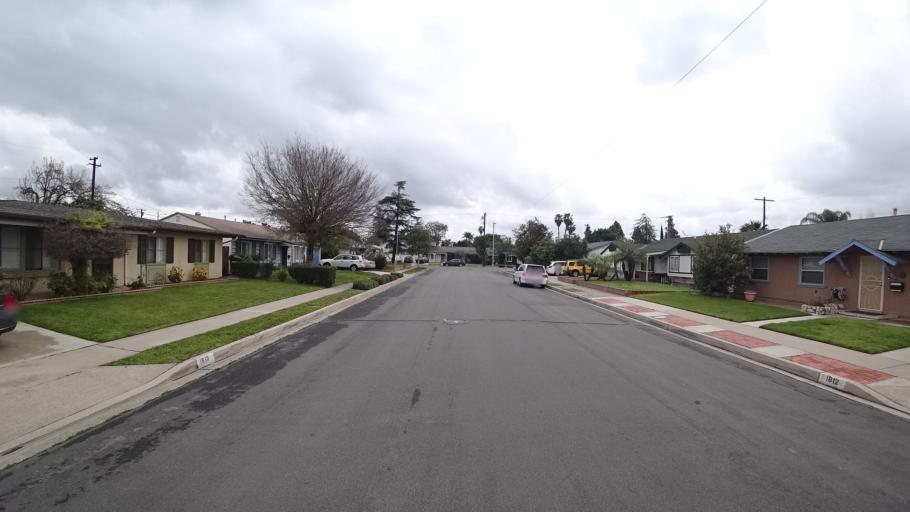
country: US
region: California
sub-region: Orange County
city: Anaheim
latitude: 33.8296
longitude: -117.9470
